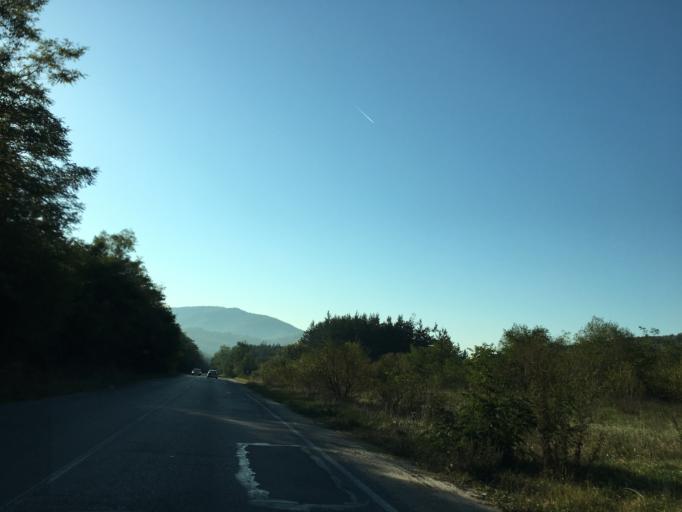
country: BG
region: Sofiya
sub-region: Obshtina Ikhtiman
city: Ikhtiman
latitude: 42.3748
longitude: 23.8784
